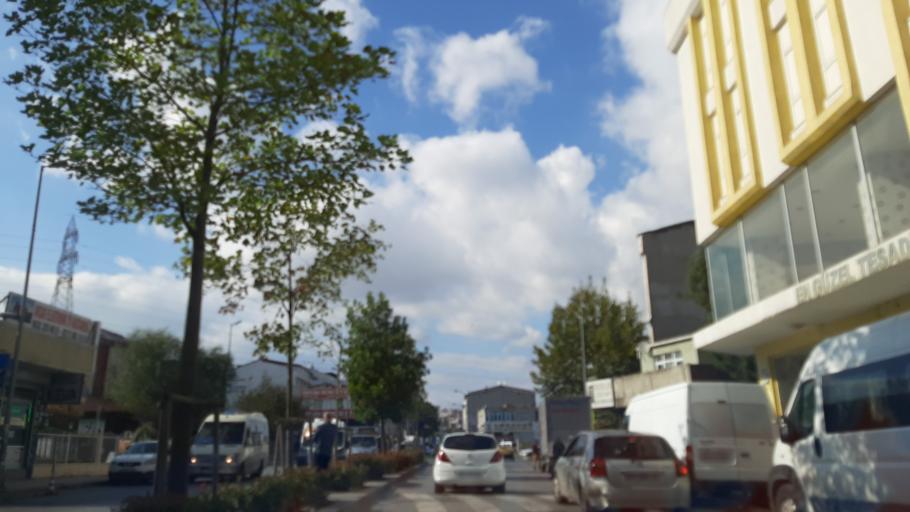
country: TR
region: Istanbul
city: Esenyurt
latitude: 41.0314
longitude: 28.6623
